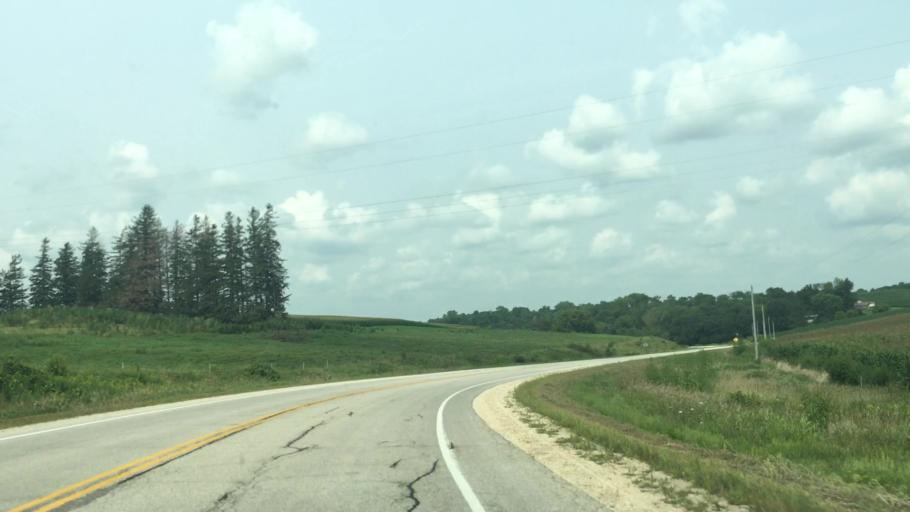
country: US
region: Minnesota
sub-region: Fillmore County
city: Preston
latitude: 43.6923
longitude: -91.9512
